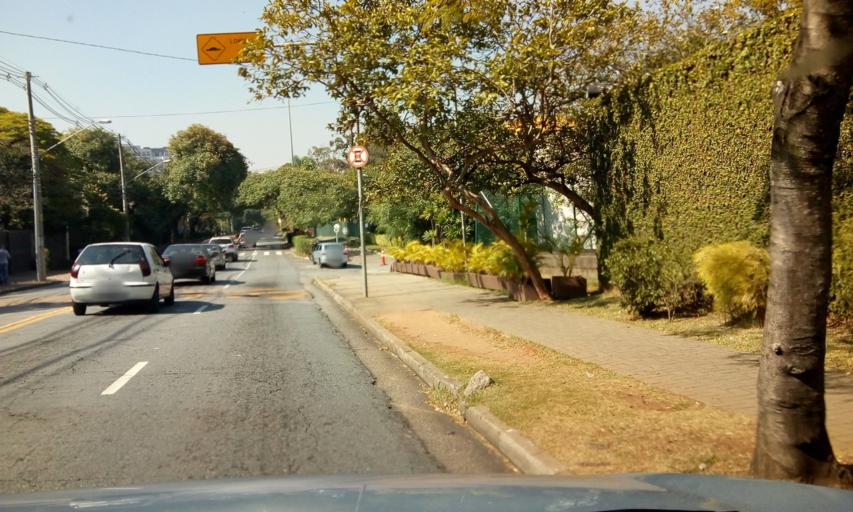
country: BR
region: Sao Paulo
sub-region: Sao Paulo
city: Sao Paulo
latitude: -23.5985
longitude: -46.7060
